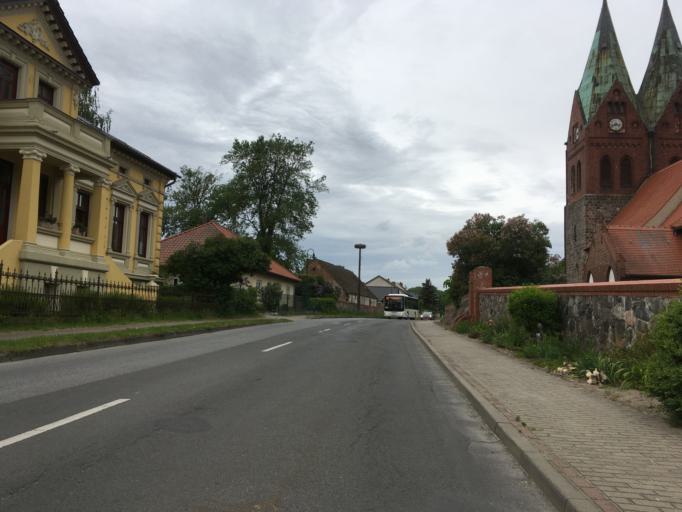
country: DE
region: Brandenburg
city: Werneuchen
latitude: 52.6634
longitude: 13.6852
